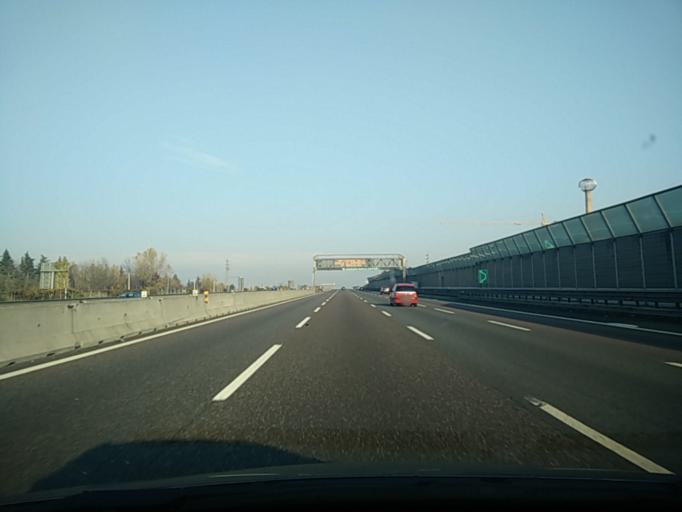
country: IT
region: Lombardy
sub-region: Provincia di Bergamo
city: Dalmine
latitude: 45.6362
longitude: 9.6066
